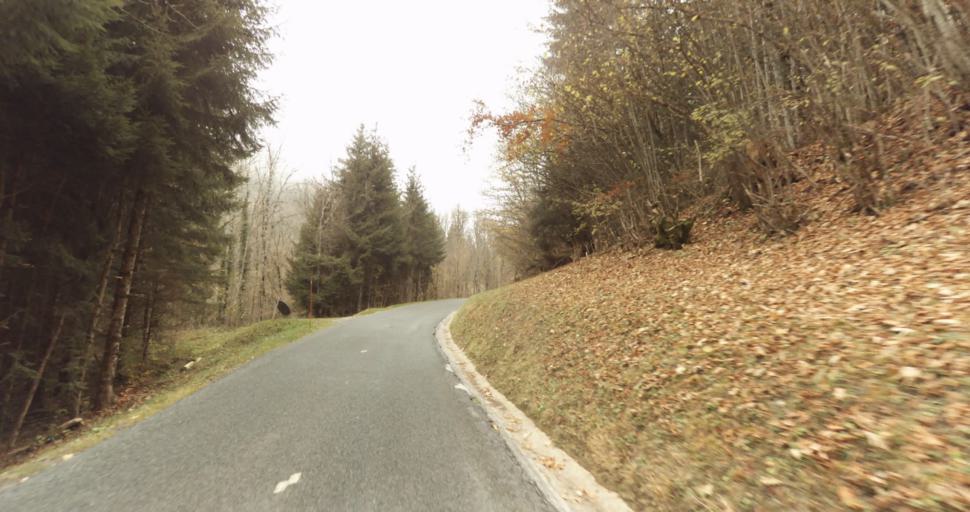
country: FR
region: Rhone-Alpes
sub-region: Departement de la Haute-Savoie
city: Doussard
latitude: 45.7936
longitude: 6.2602
